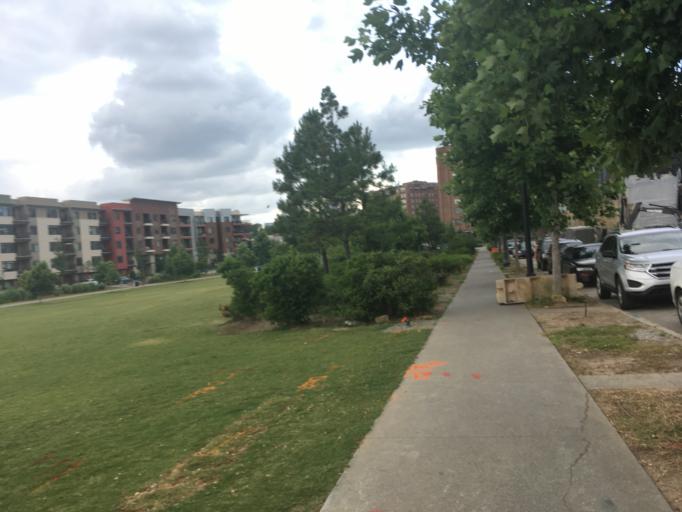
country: US
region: Georgia
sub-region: DeKalb County
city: Druid Hills
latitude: 33.7699
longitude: -84.3643
